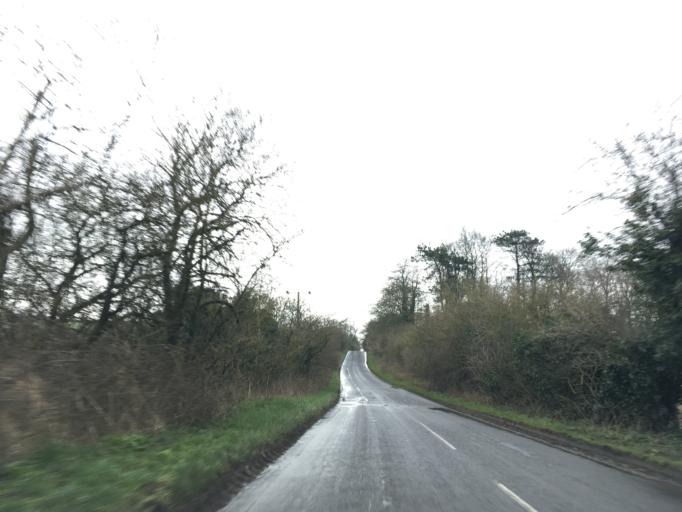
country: GB
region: England
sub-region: Borough of Swindon
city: Wanborough
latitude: 51.5370
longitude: -1.6774
